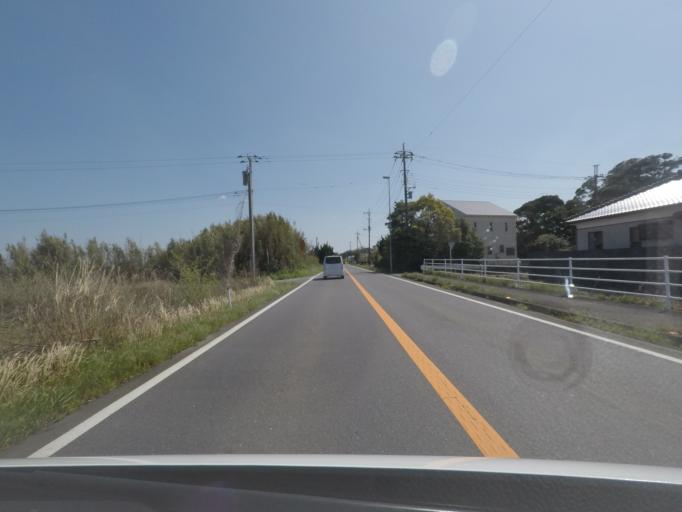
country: JP
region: Chiba
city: Asahi
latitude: 35.7943
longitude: 140.7228
